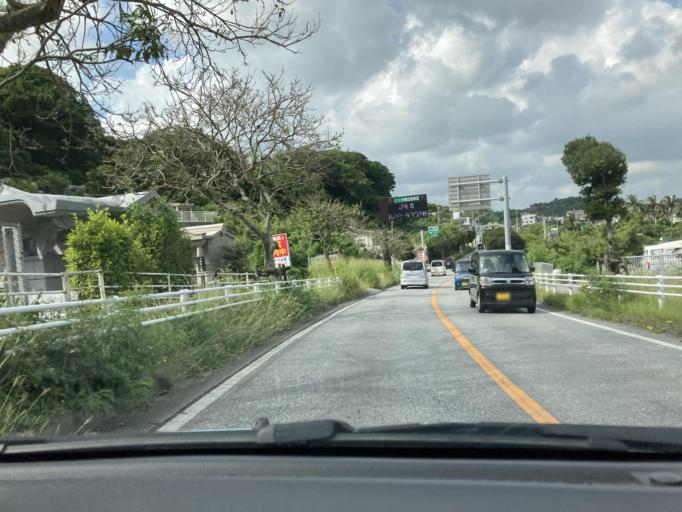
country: JP
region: Okinawa
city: Chatan
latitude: 26.2904
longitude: 127.7850
